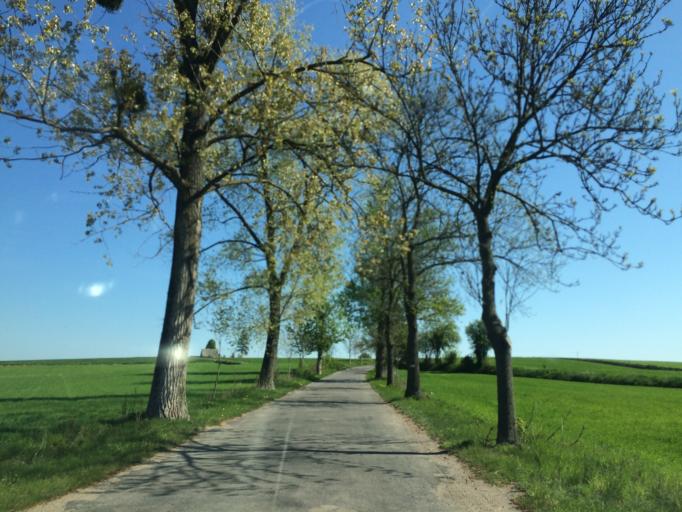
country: PL
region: Warmian-Masurian Voivodeship
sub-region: Powiat nowomiejski
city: Kurzetnik
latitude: 53.4679
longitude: 19.4756
